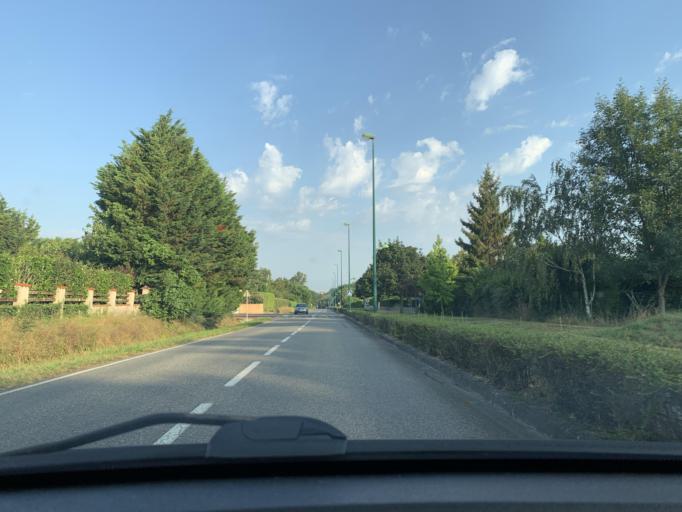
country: FR
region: Midi-Pyrenees
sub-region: Departement de la Haute-Garonne
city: Labege
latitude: 43.5314
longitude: 1.5504
